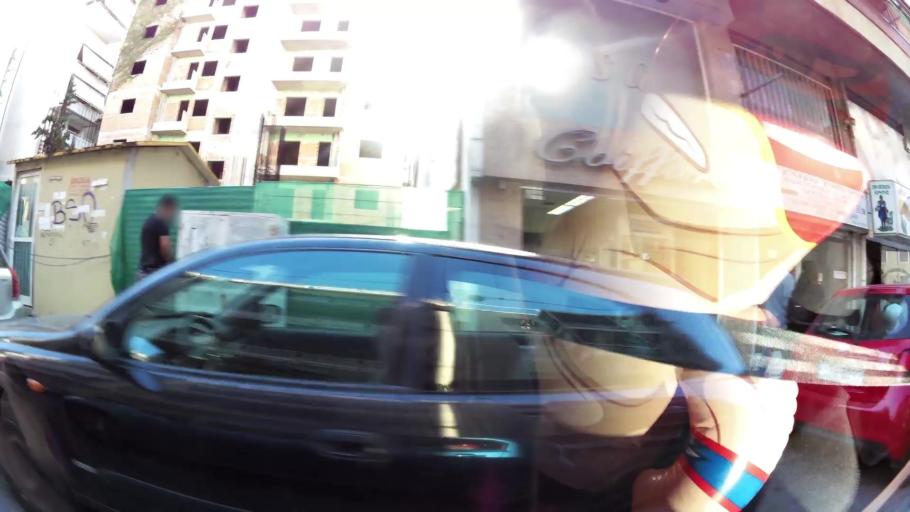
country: GR
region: Attica
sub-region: Nomarchia Athinas
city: Kaisariani
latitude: 37.9877
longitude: 23.7644
